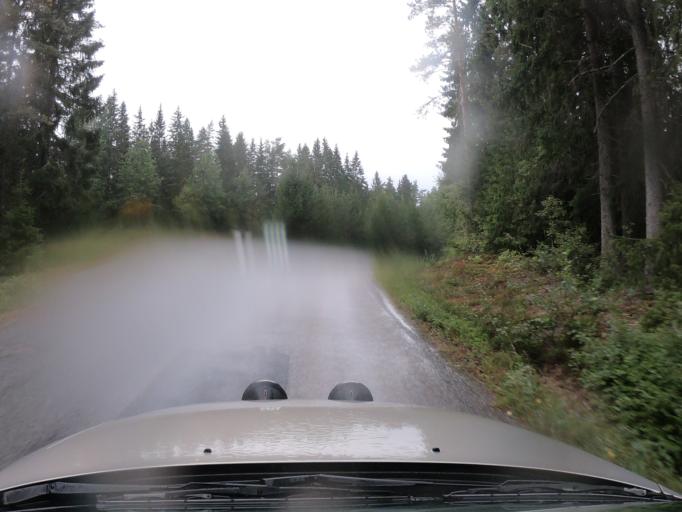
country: SE
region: Joenkoeping
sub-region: Vetlanda Kommun
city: Landsbro
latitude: 57.2762
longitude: 14.8328
